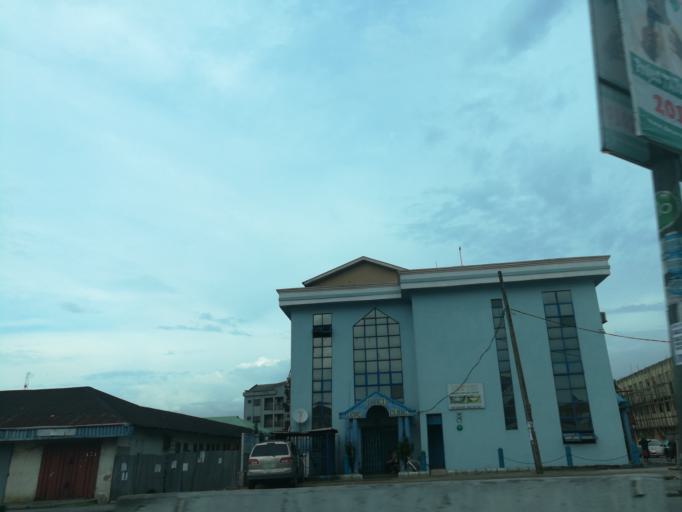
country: NG
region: Rivers
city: Port Harcourt
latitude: 4.8006
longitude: 7.0065
